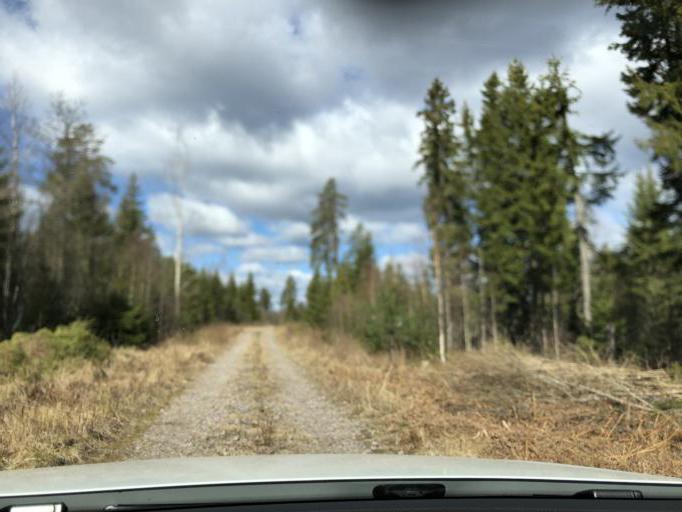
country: SE
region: Uppsala
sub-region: Tierps Kommun
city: Tierp
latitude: 60.3297
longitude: 17.3407
